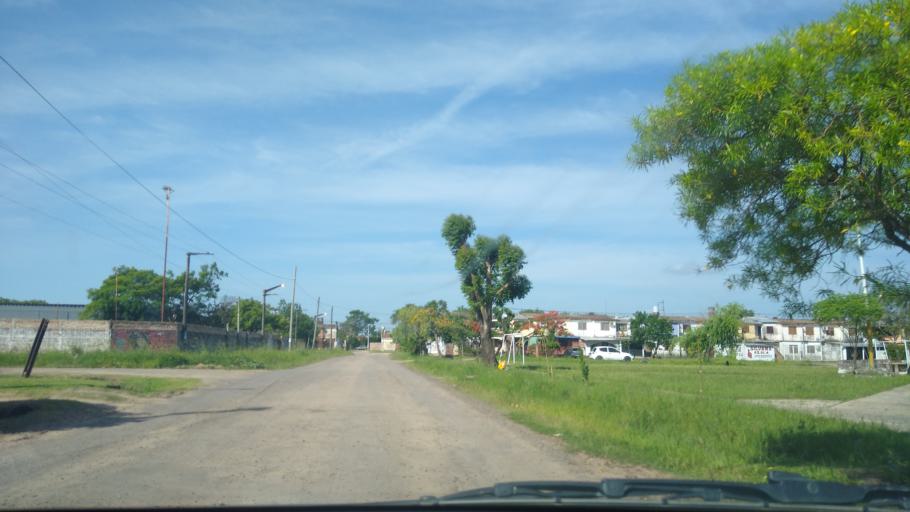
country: AR
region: Chaco
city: Puerto Vilelas
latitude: -27.4982
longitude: -58.9551
